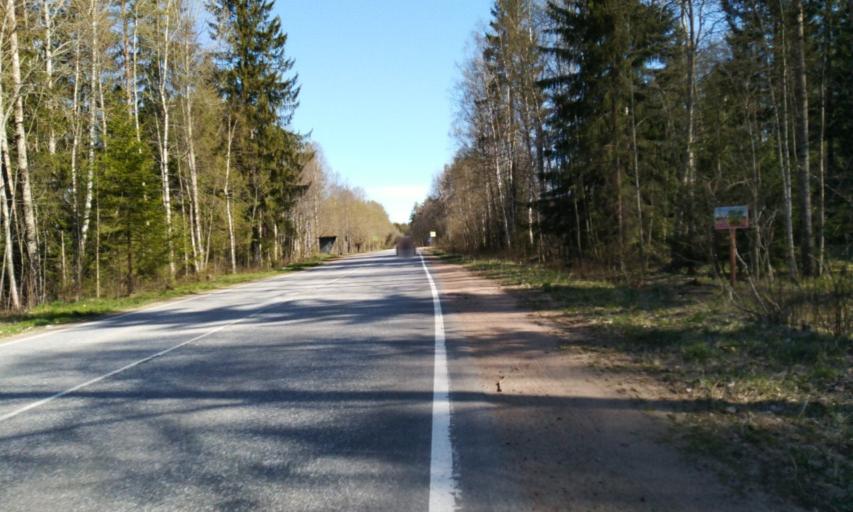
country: RU
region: Leningrad
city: Garbolovo
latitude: 60.3498
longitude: 30.4432
